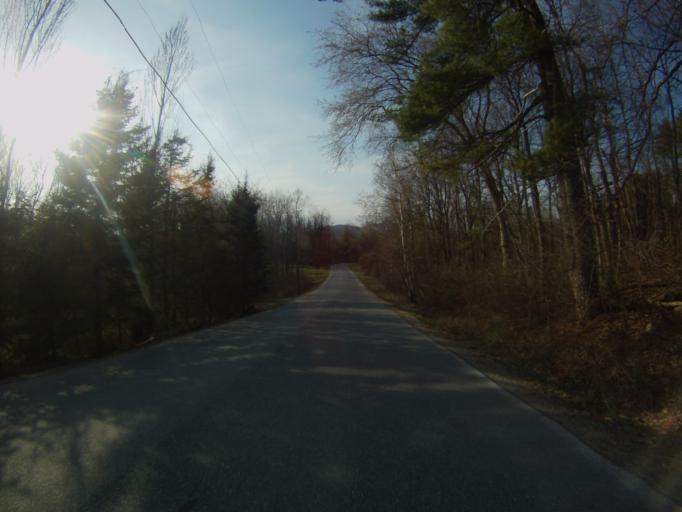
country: US
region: Vermont
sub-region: Addison County
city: Middlebury (village)
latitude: 44.0090
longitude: -73.2171
